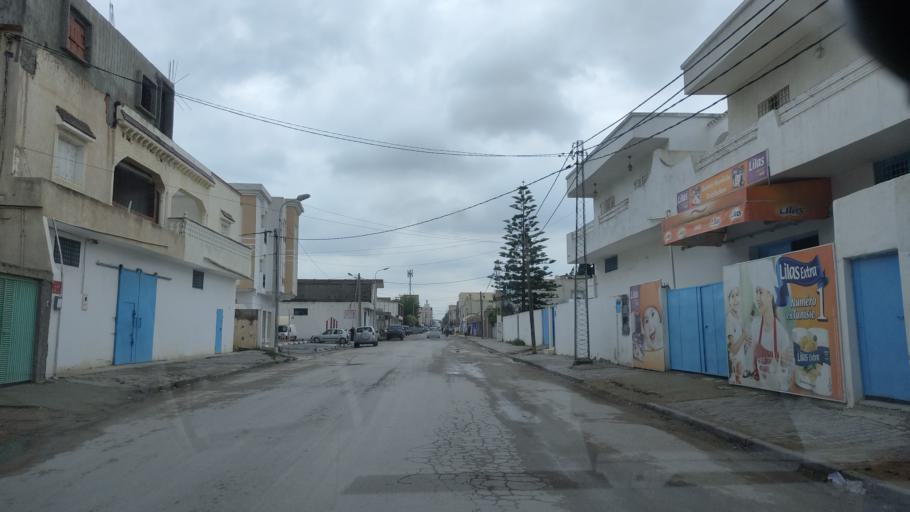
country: TN
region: Ariana
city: Ariana
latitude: 36.8766
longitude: 10.2175
